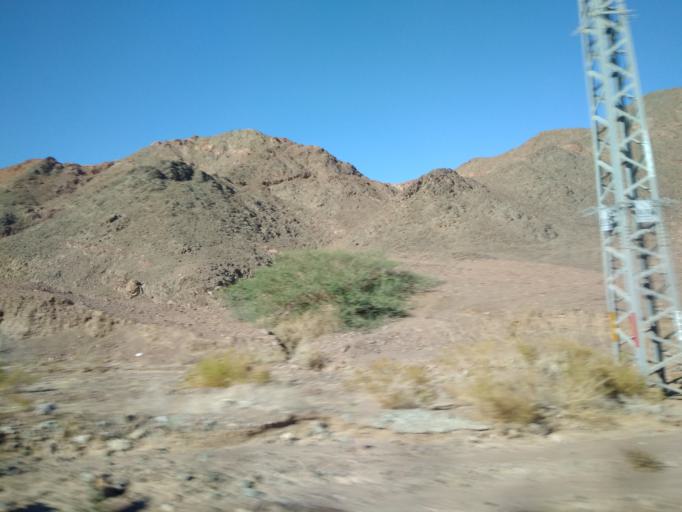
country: IL
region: Southern District
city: Eilat
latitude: 29.5553
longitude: 34.9246
